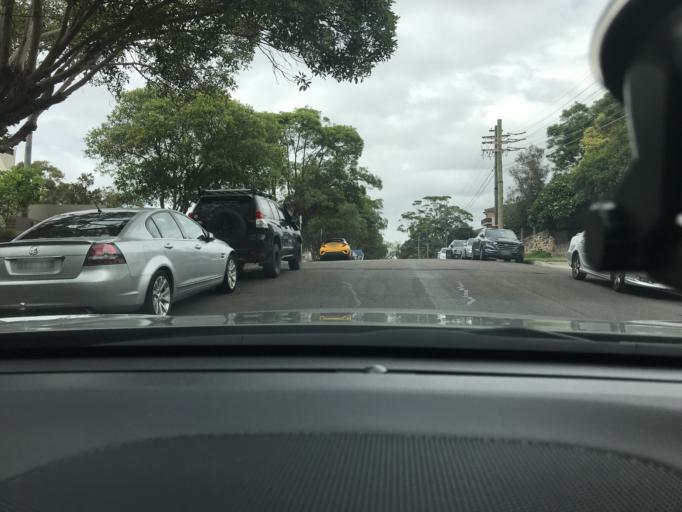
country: AU
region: New South Wales
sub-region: Canada Bay
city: Wareemba
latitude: -33.8467
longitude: 151.1311
